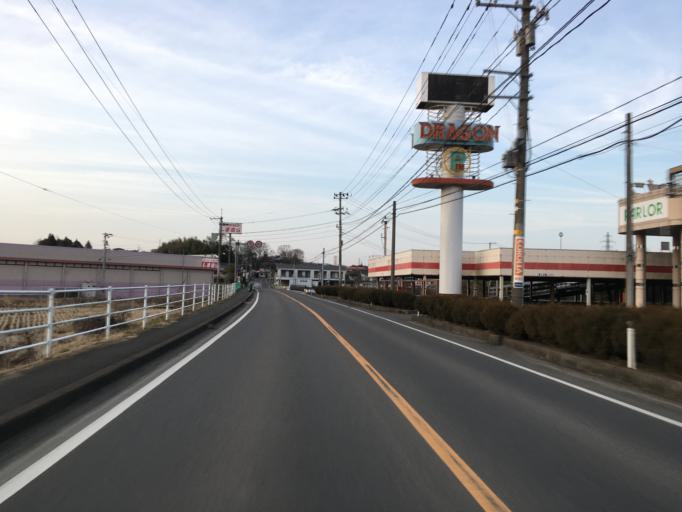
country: JP
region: Fukushima
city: Ishikawa
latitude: 37.0190
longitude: 140.3915
